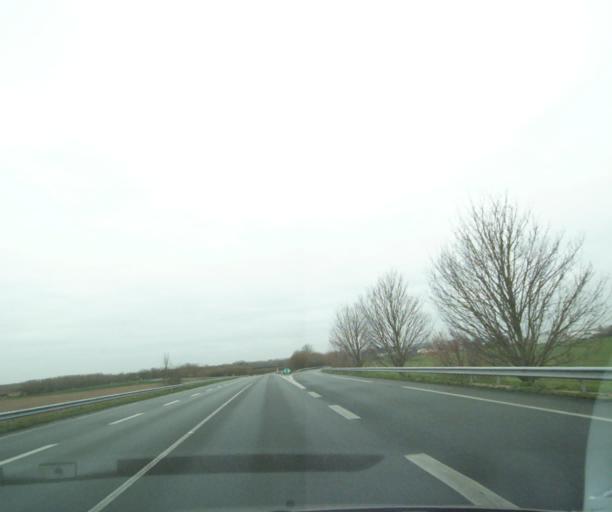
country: FR
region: Picardie
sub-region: Departement de l'Oise
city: Noyon
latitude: 49.5768
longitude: 3.0389
